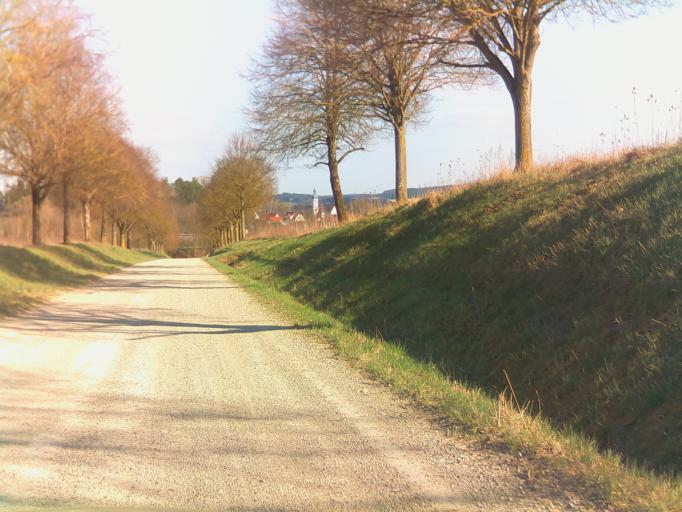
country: DE
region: Bavaria
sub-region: Swabia
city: Pottmes
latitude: 48.5895
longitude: 11.0764
